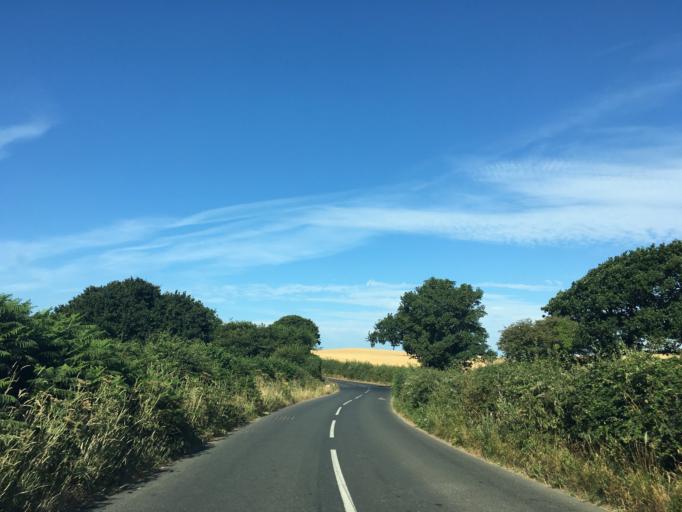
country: GB
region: England
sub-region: Isle of Wight
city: Niton
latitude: 50.6230
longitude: -1.2921
